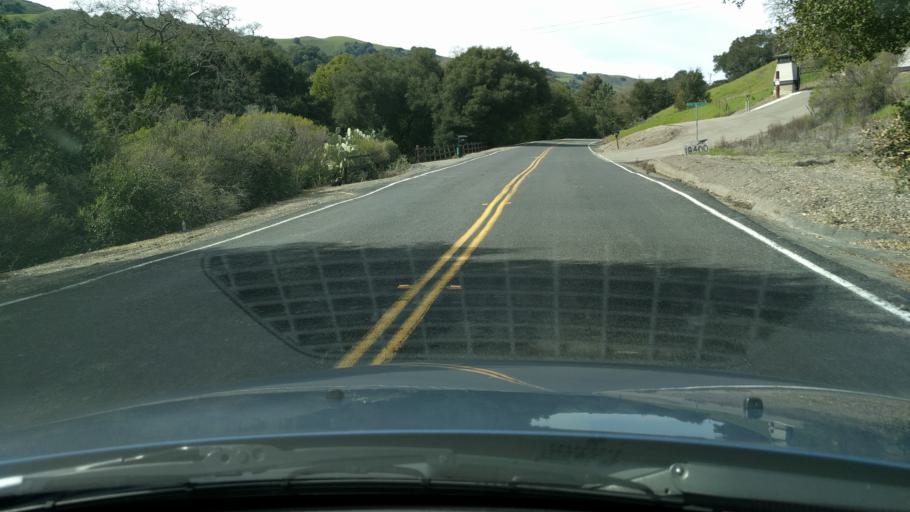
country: US
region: California
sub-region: Contra Costa County
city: Danville
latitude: 37.7974
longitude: -122.0253
